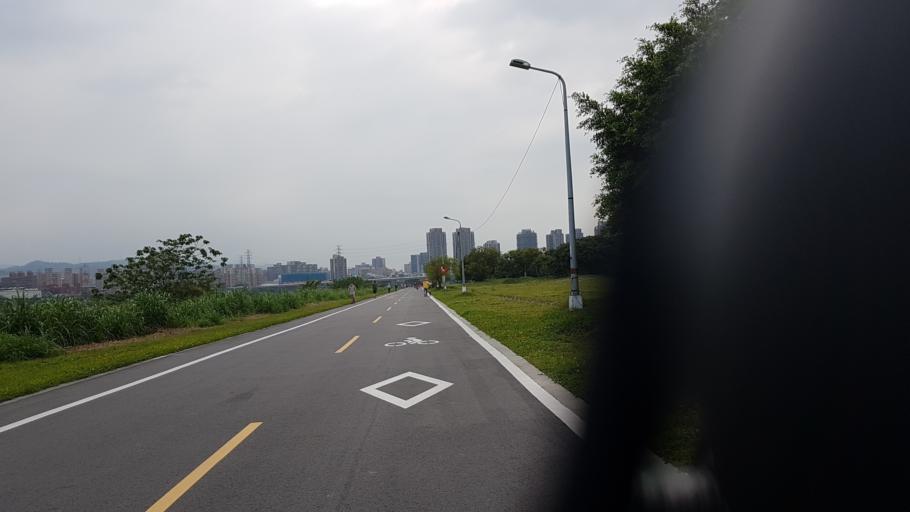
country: TW
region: Taipei
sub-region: Taipei
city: Banqiao
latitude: 25.0162
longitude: 121.5022
